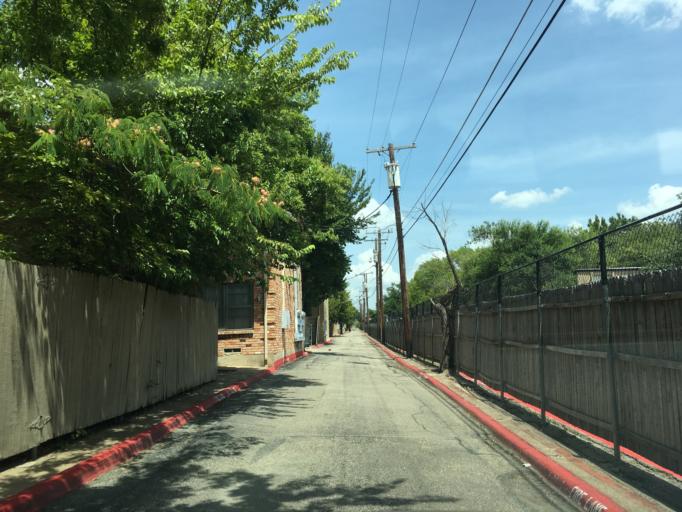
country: US
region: Texas
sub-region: Dallas County
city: Farmers Branch
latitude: 32.9112
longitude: -96.8588
